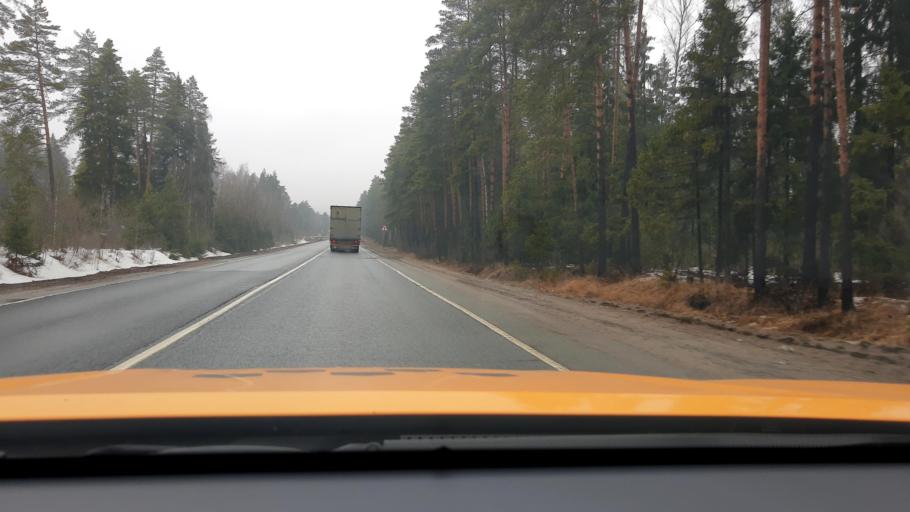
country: RU
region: Moskovskaya
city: Chernogolovka
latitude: 55.9908
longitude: 38.3282
